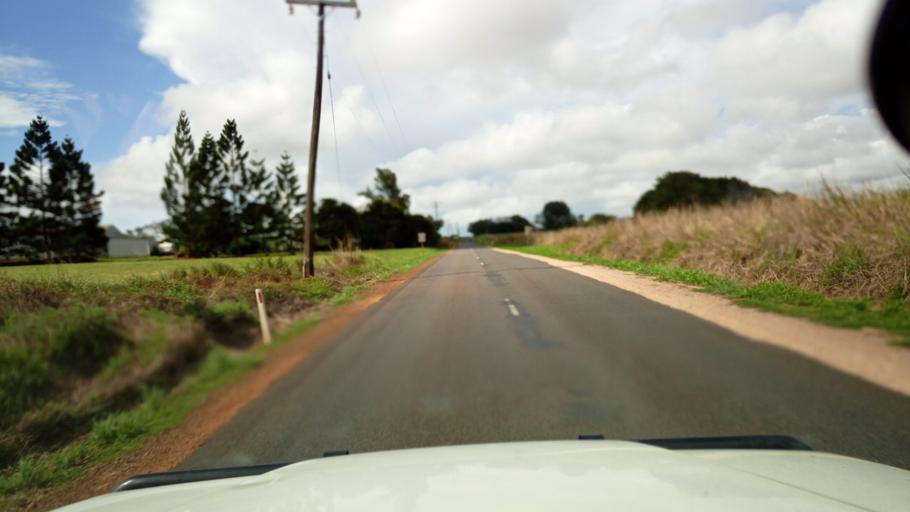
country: AU
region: Queensland
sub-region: Tablelands
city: Tolga
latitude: -17.2227
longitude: 145.5376
